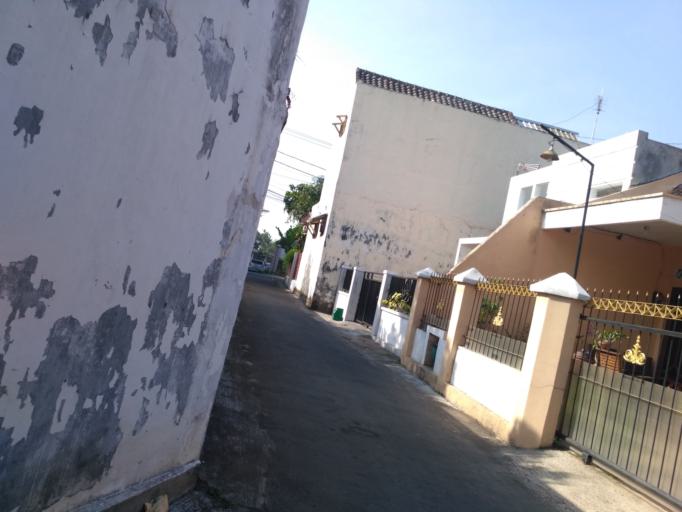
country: ID
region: East Java
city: Malang
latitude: -7.9517
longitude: 112.6220
